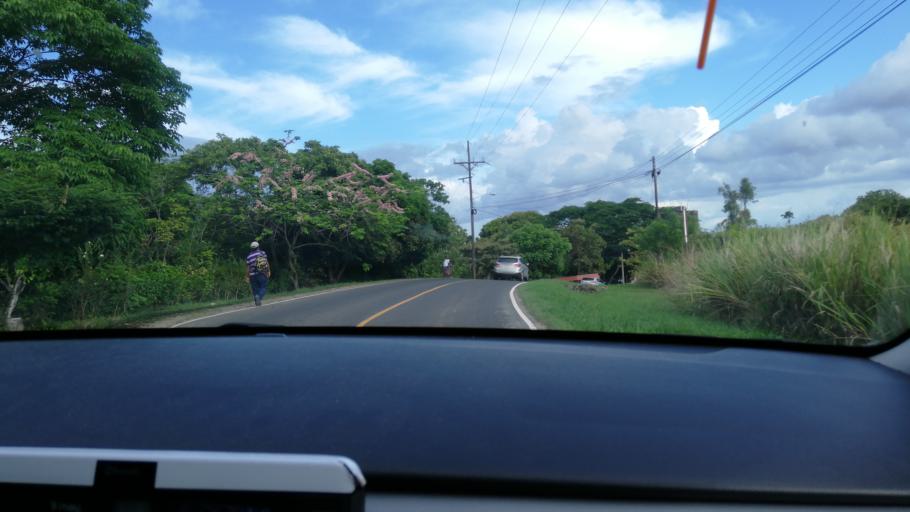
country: PA
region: Panama
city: Las Colinas
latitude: 8.5163
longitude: -80.0354
